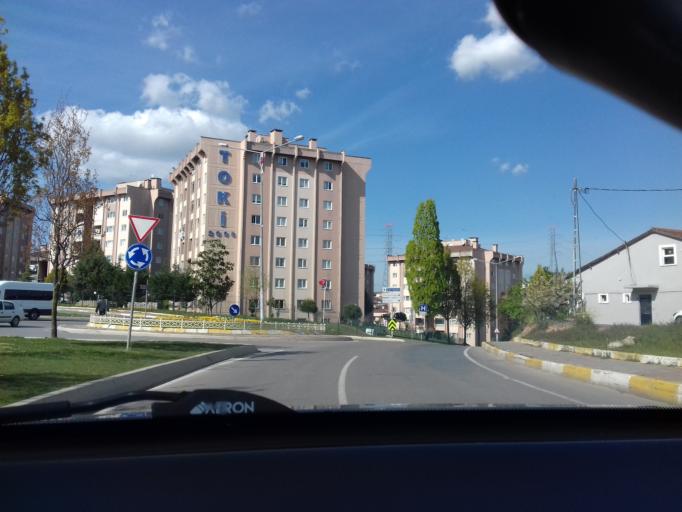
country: TR
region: Istanbul
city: Pendik
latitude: 40.9083
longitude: 29.2787
